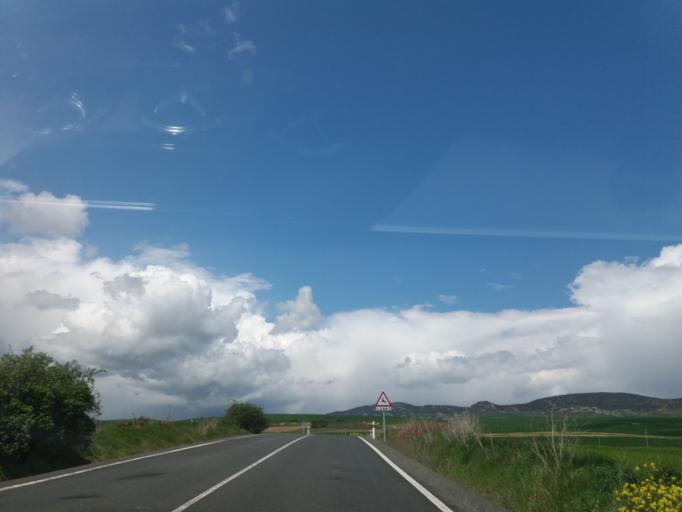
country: ES
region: La Rioja
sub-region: Provincia de La Rioja
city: Fonzaleche
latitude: 42.5829
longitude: -3.0280
